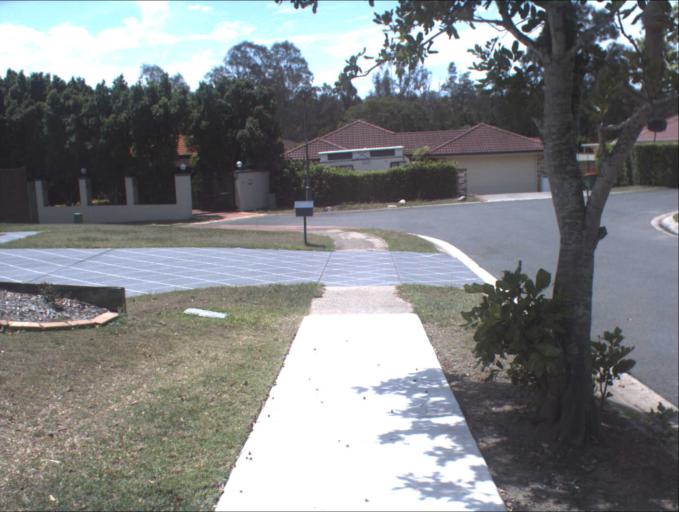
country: AU
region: Queensland
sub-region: Logan
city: Slacks Creek
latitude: -27.6417
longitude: 153.1459
